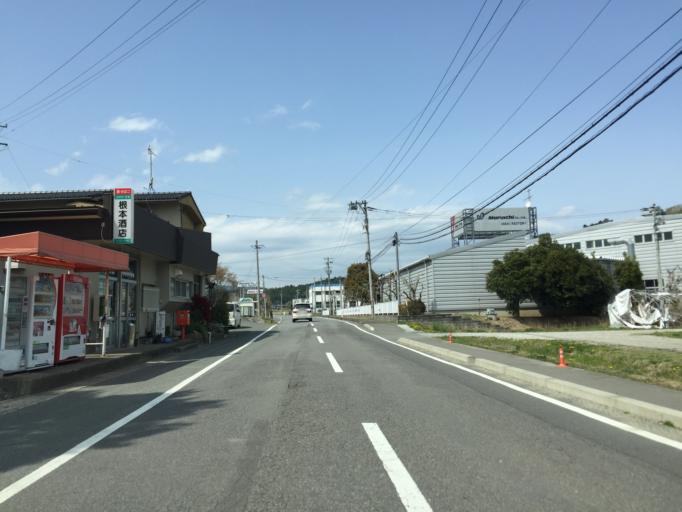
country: JP
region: Fukushima
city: Iwaki
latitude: 37.1590
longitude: 140.9756
